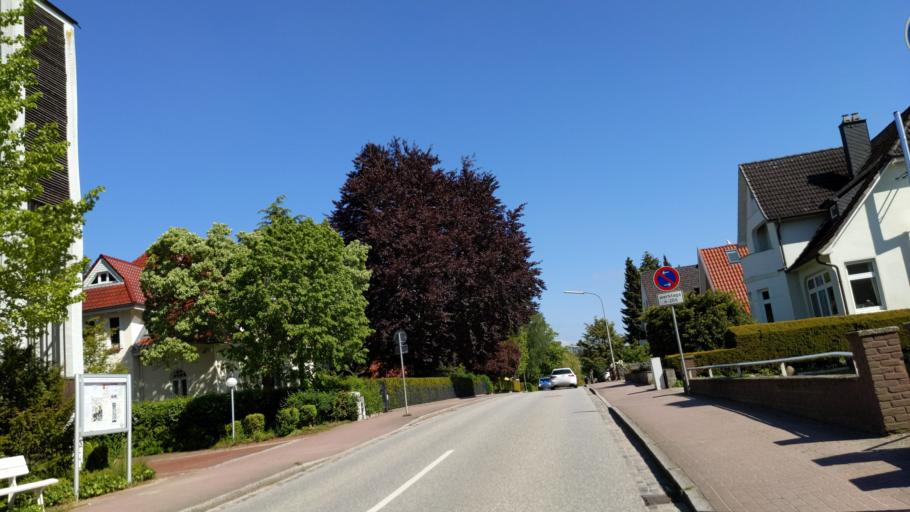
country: DE
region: Schleswig-Holstein
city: Malente
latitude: 54.1652
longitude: 10.5619
